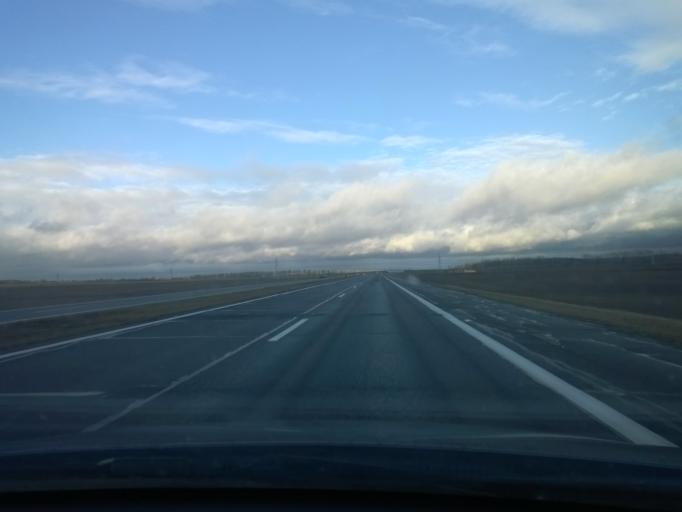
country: BY
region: Brest
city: Baranovichi
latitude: 53.2262
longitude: 26.1613
